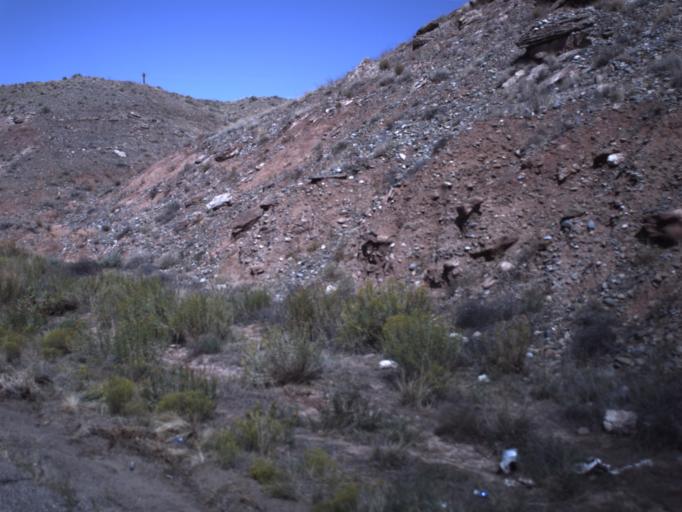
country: US
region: Colorado
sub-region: Montezuma County
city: Towaoc
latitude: 37.2240
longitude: -109.2054
